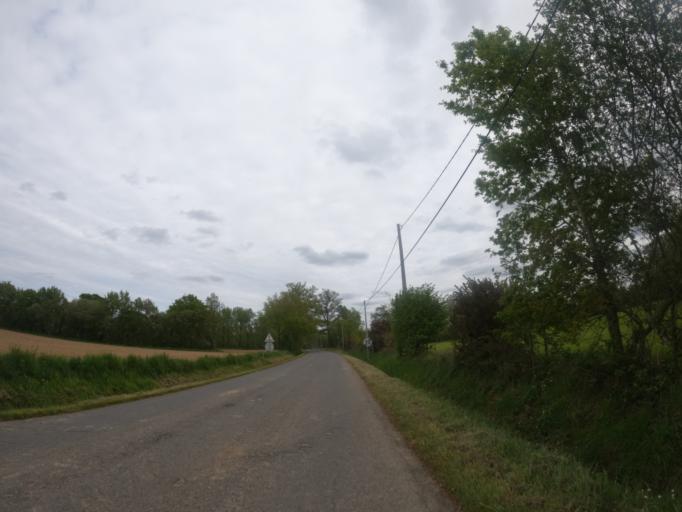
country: FR
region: Pays de la Loire
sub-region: Departement de la Loire-Atlantique
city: Rouge
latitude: 47.7380
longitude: -1.4372
